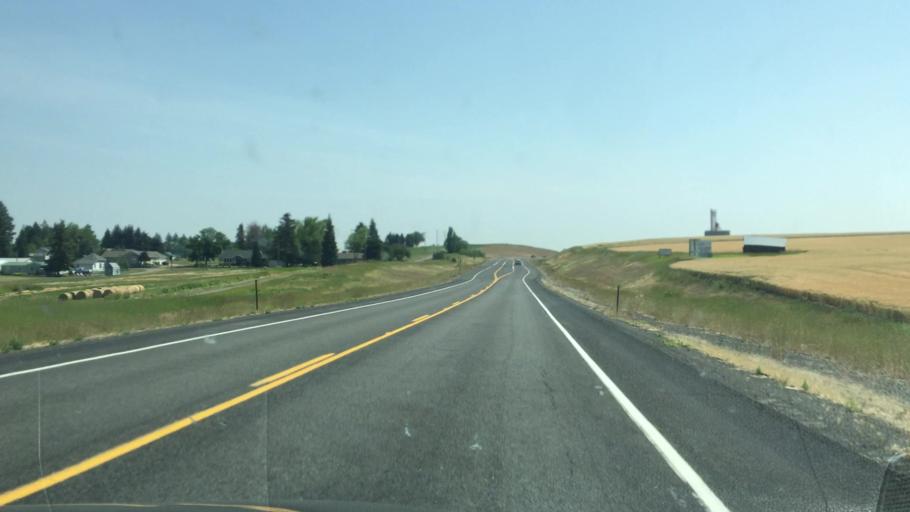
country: US
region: Idaho
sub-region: Lewis County
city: Nezperce
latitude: 46.2377
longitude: -116.4773
